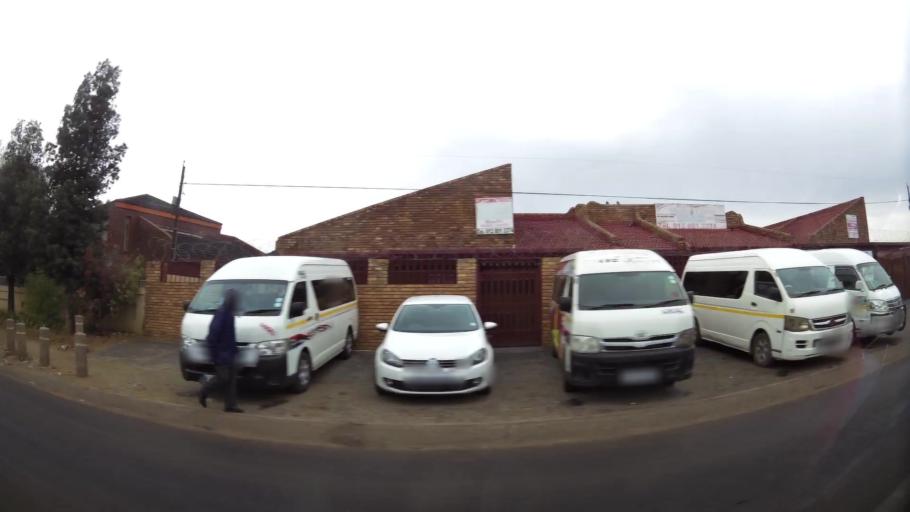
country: ZA
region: Gauteng
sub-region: City of Tshwane Metropolitan Municipality
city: Cullinan
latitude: -25.7185
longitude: 28.3662
